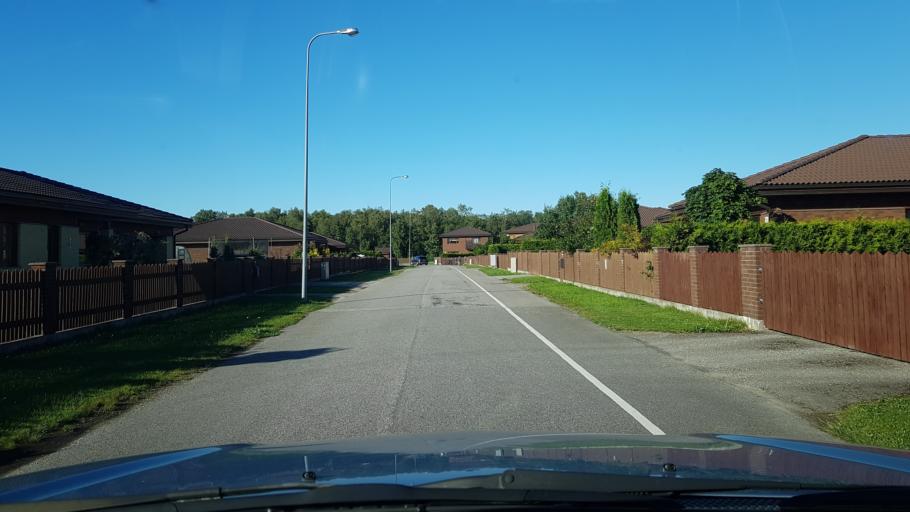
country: EE
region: Harju
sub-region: Rae vald
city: Jueri
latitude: 59.3878
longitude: 24.8575
